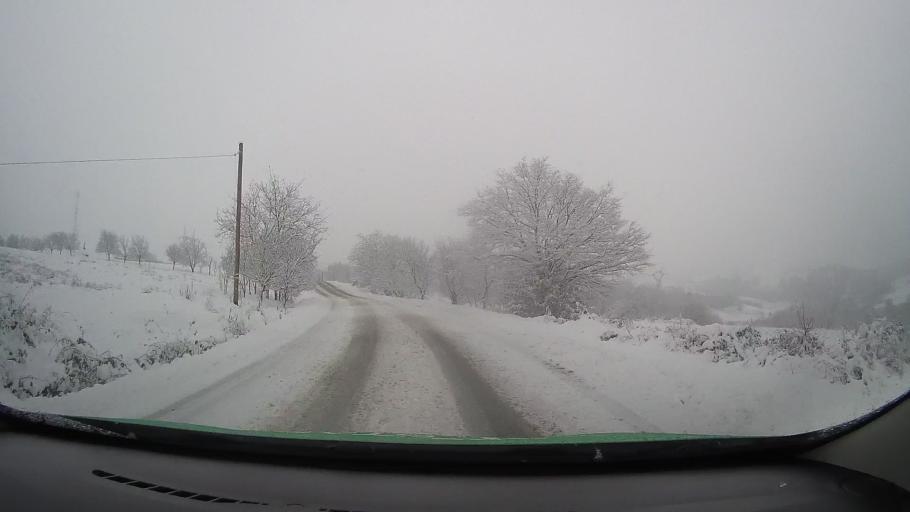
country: RO
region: Hunedoara
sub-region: Comuna Teliucu Inferior
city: Teliucu Inferior
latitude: 45.7037
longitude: 22.8819
